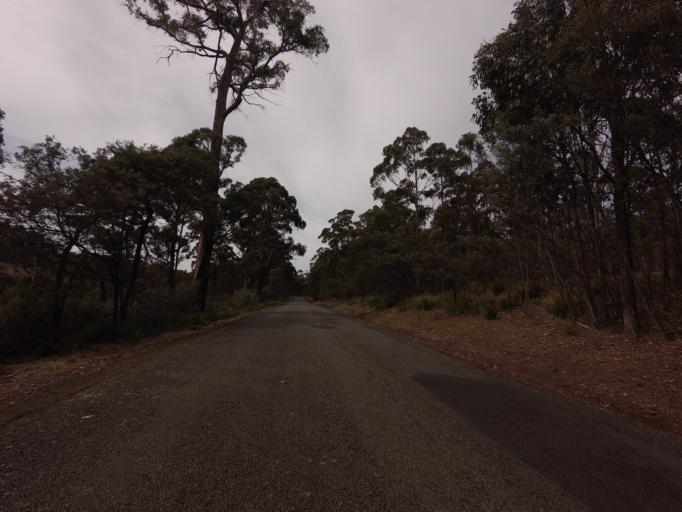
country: AU
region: Tasmania
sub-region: Sorell
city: Sorell
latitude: -42.5352
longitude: 147.6550
